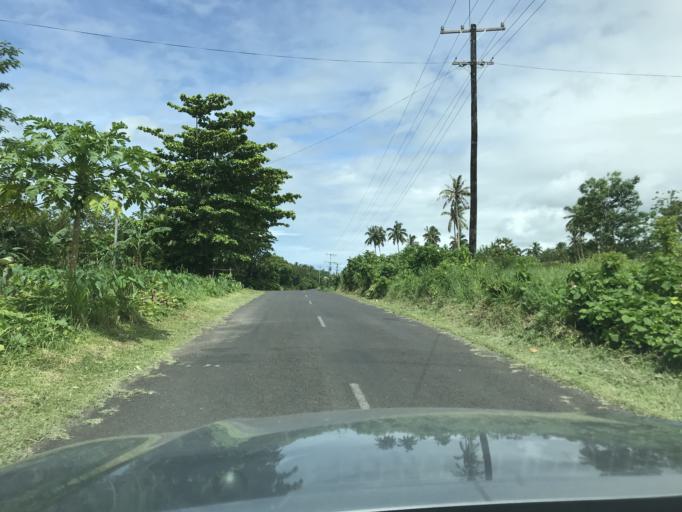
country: WS
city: Fasito`outa
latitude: -13.8578
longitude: -171.8978
